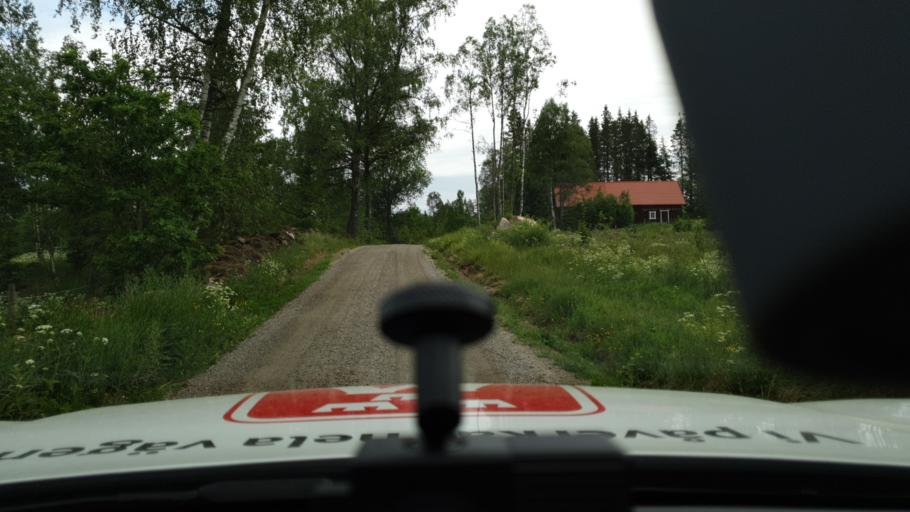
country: SE
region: Vaestra Goetaland
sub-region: Falkopings Kommun
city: Falkoeping
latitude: 58.0292
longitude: 13.6709
